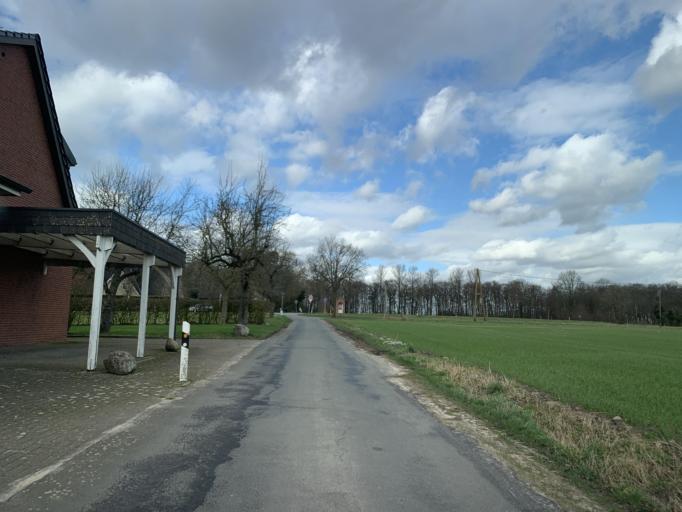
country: DE
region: North Rhine-Westphalia
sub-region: Regierungsbezirk Munster
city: Horstmar
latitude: 52.0885
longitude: 7.3156
